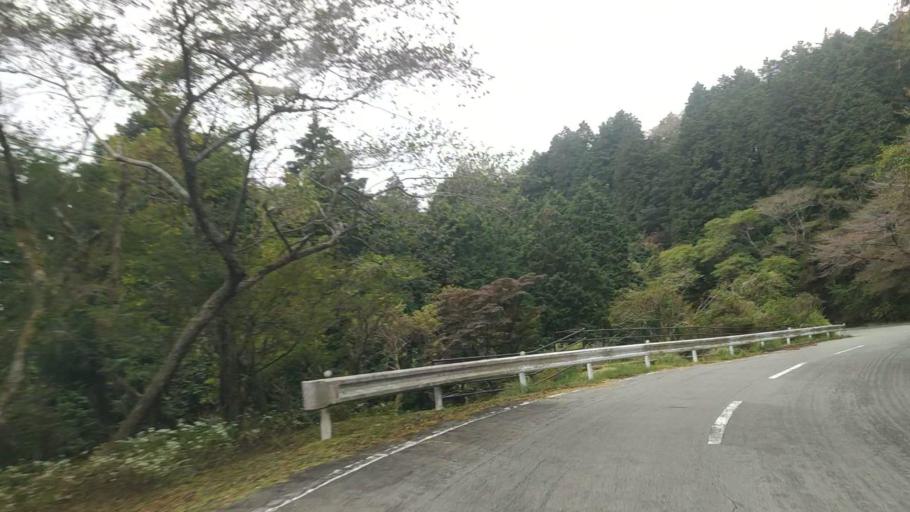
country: JP
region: Shizuoka
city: Heda
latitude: 34.9333
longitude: 138.8356
